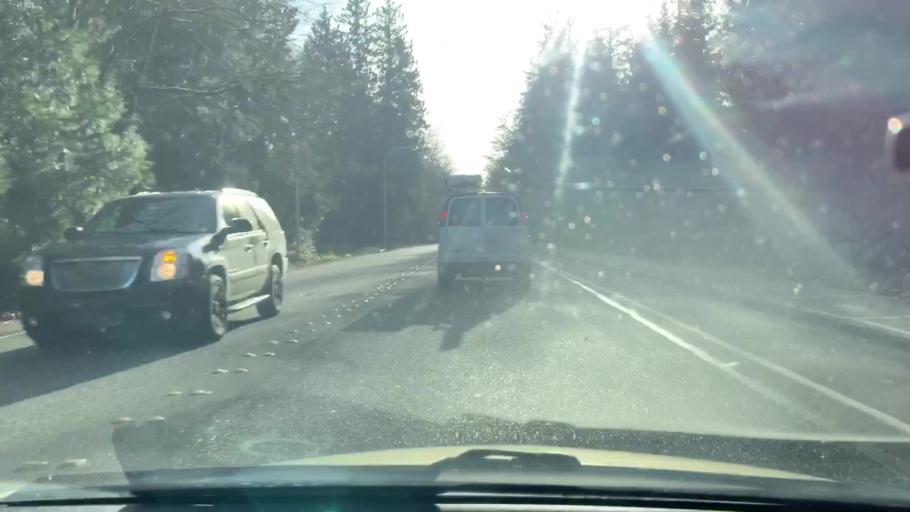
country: US
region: Washington
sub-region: King County
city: Bellevue
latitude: 47.6315
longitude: -122.1910
